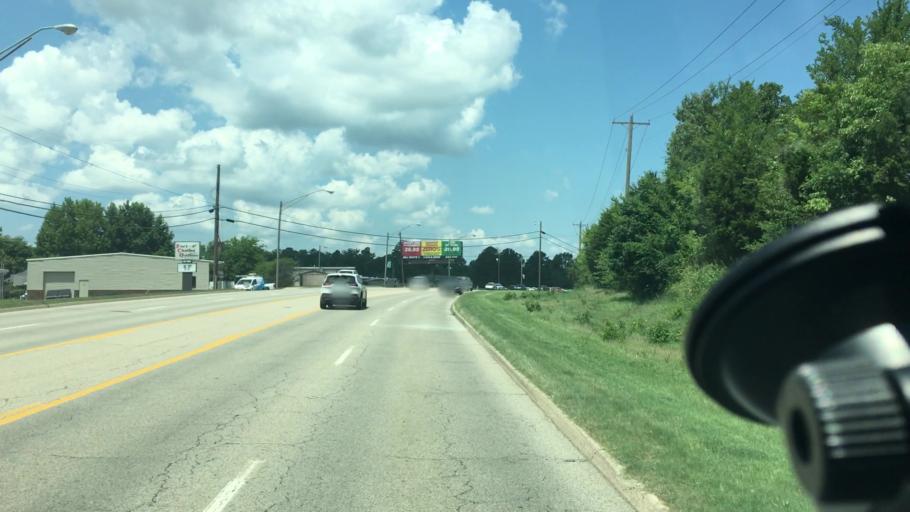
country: US
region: Arkansas
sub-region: Sebastian County
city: Barling
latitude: 35.3362
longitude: -94.3169
